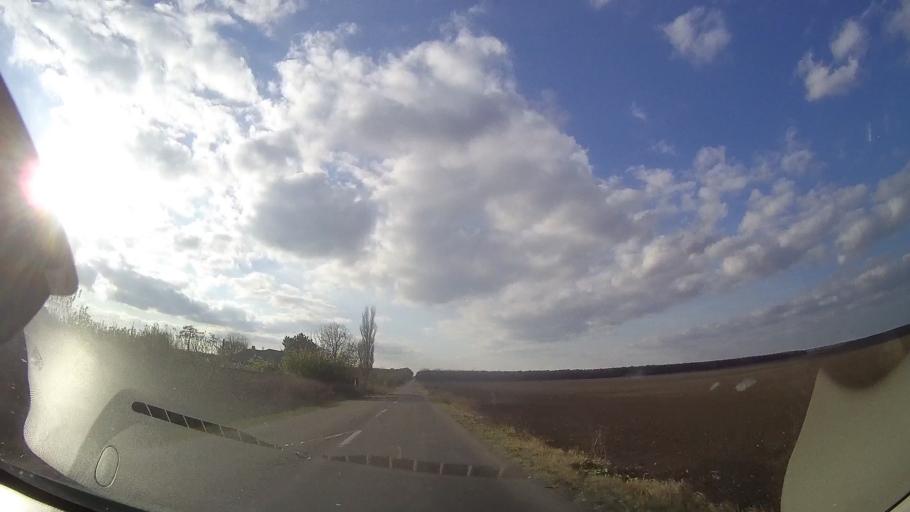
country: RO
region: Constanta
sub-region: Comuna Comana
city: Comana
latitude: 43.8192
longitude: 28.2907
